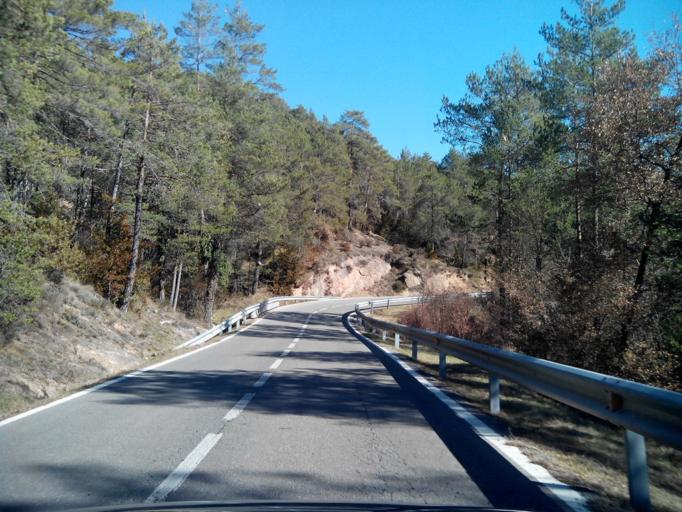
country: ES
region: Catalonia
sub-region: Provincia de Barcelona
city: Vilada
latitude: 42.1307
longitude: 1.9407
